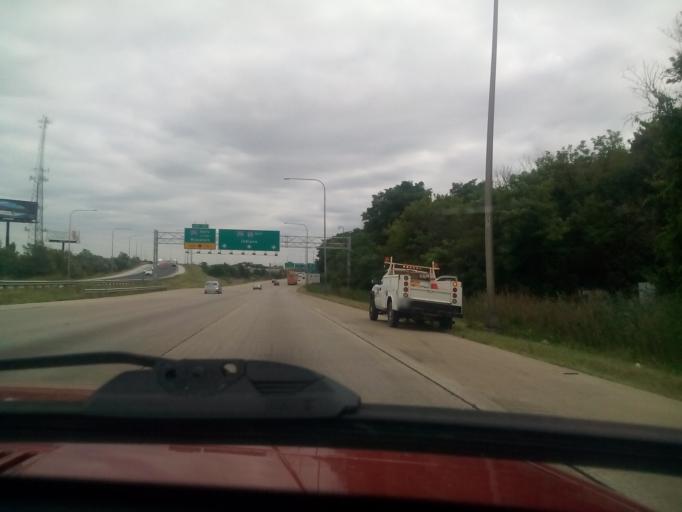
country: US
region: Illinois
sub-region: Cook County
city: University Park
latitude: 41.5829
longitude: -87.6899
